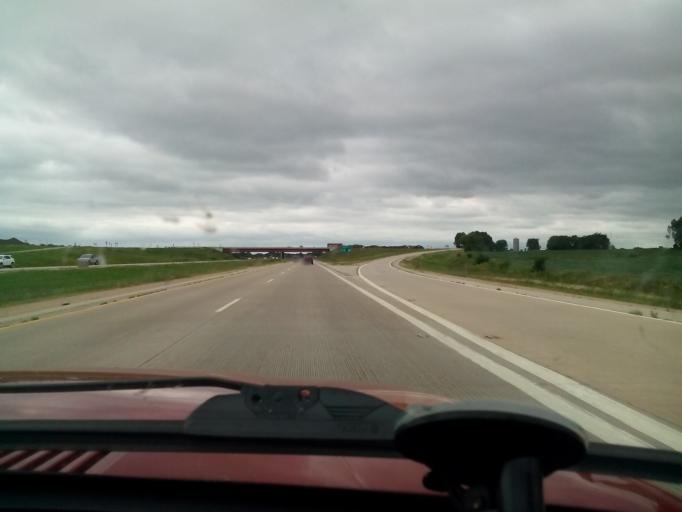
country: US
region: Wisconsin
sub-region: Columbia County
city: Columbus
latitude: 43.3213
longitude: -89.0455
